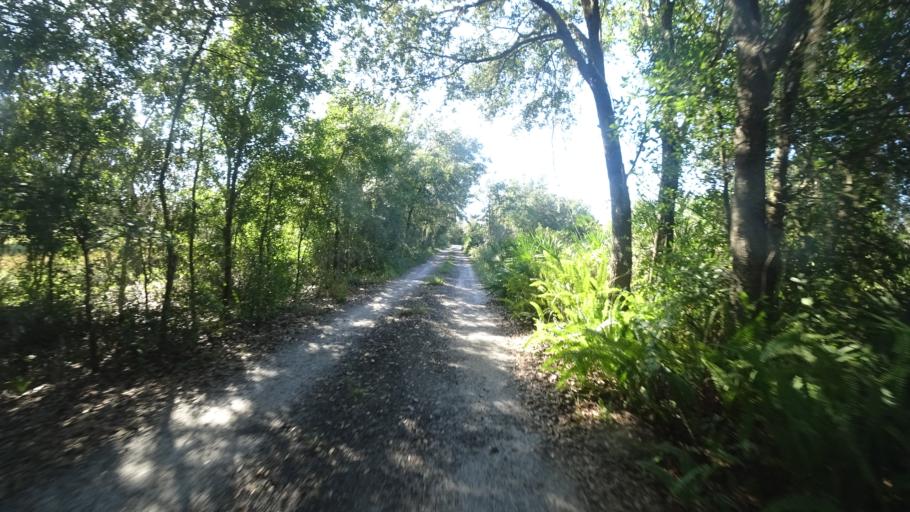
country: US
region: Florida
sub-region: Sarasota County
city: The Meadows
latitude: 27.4284
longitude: -82.2554
